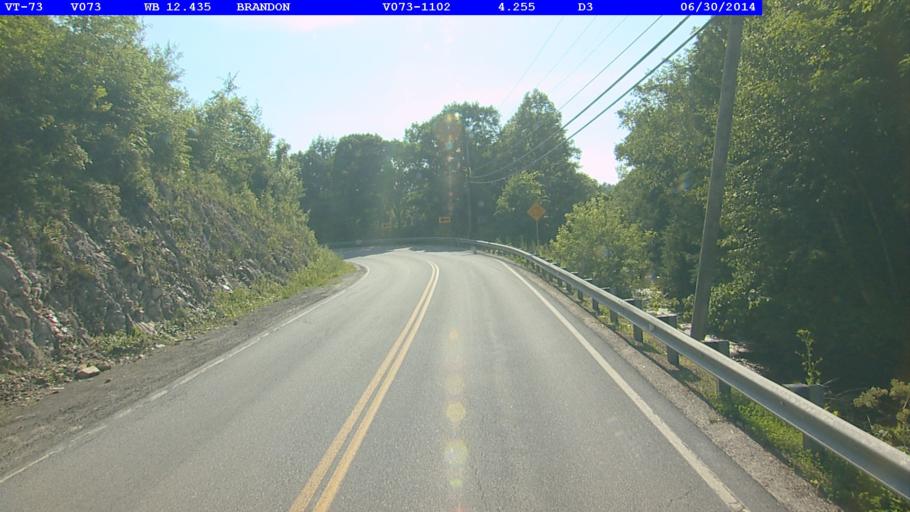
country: US
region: Vermont
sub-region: Rutland County
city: Brandon
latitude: 43.8103
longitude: -73.0752
